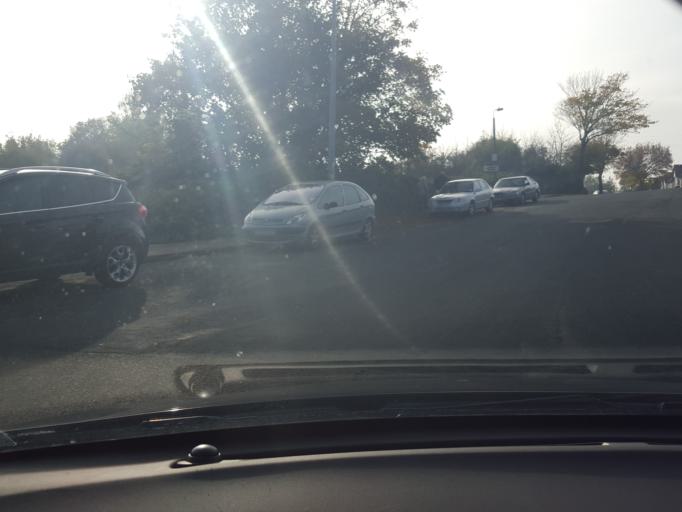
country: GB
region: England
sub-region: Essex
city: Harwich
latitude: 51.9408
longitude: 1.2903
